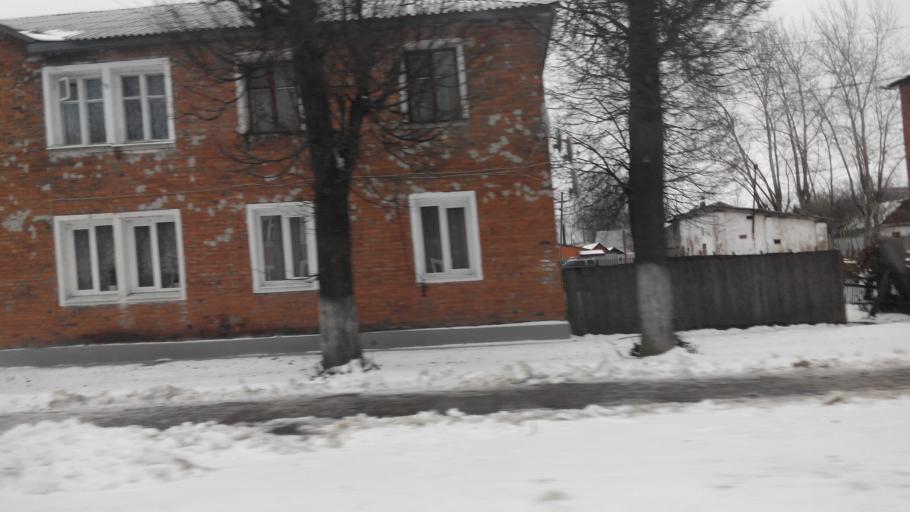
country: RU
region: Tula
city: Uzlovaya
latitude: 53.9632
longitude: 38.1644
